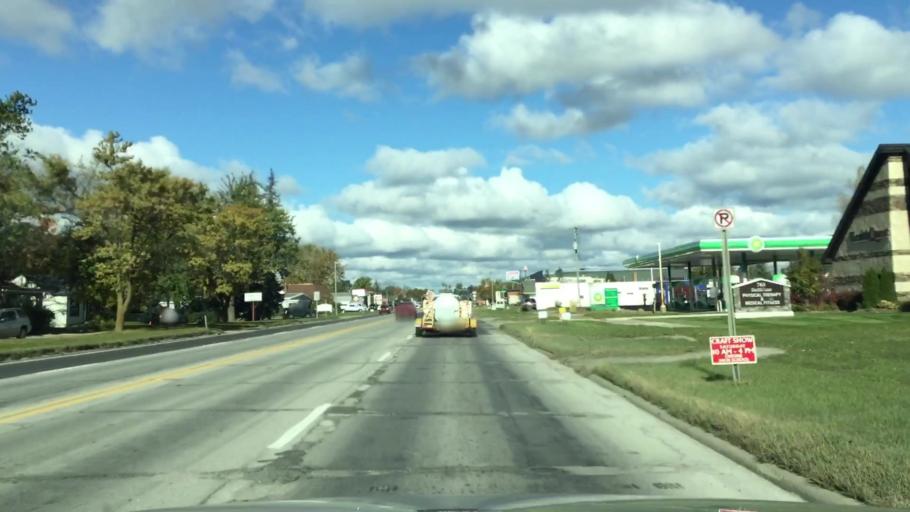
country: US
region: Michigan
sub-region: Oakland County
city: Oxford
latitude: 42.8141
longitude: -83.2551
